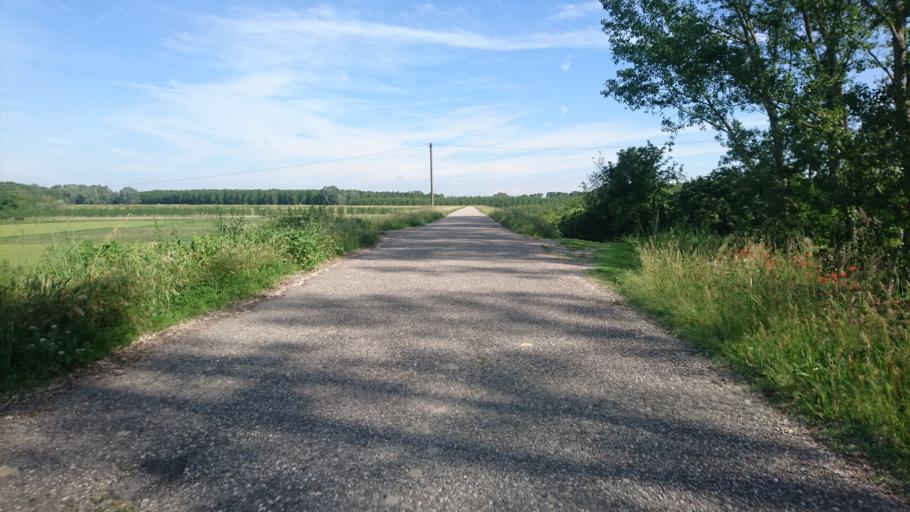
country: IT
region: Veneto
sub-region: Provincia di Rovigo
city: Bergantino
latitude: 45.0465
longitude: 11.2631
